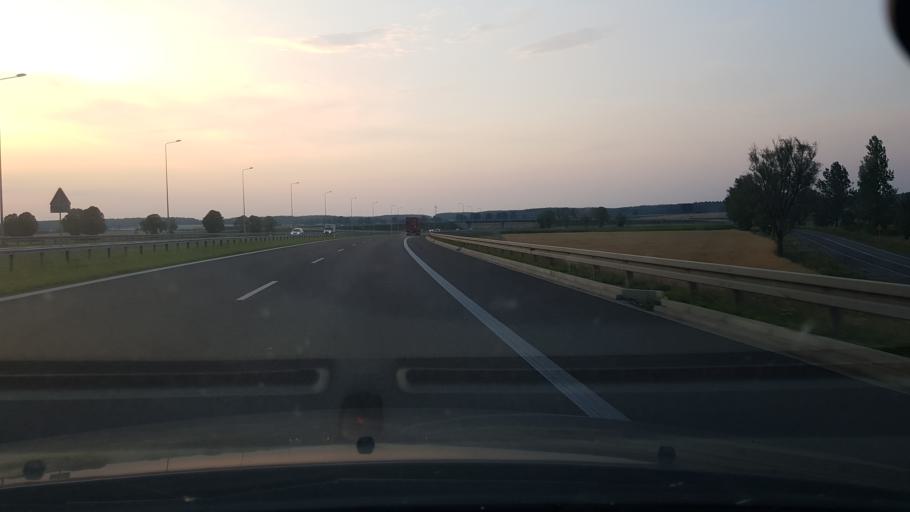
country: PL
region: Masovian Voivodeship
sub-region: Powiat mlawski
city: Wieczfnia Koscielna
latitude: 53.2229
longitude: 20.4223
